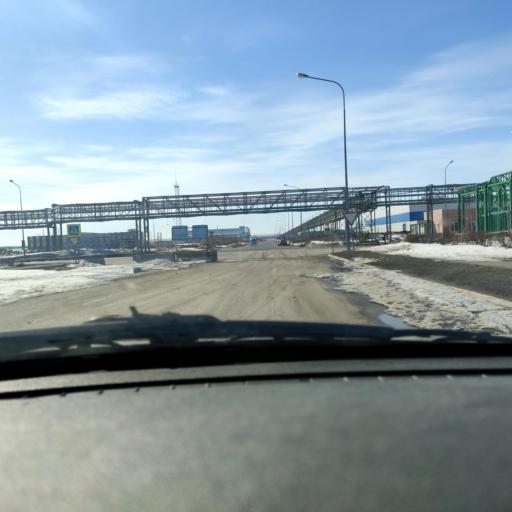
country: RU
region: Samara
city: Podstepki
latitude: 53.5610
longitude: 49.1847
